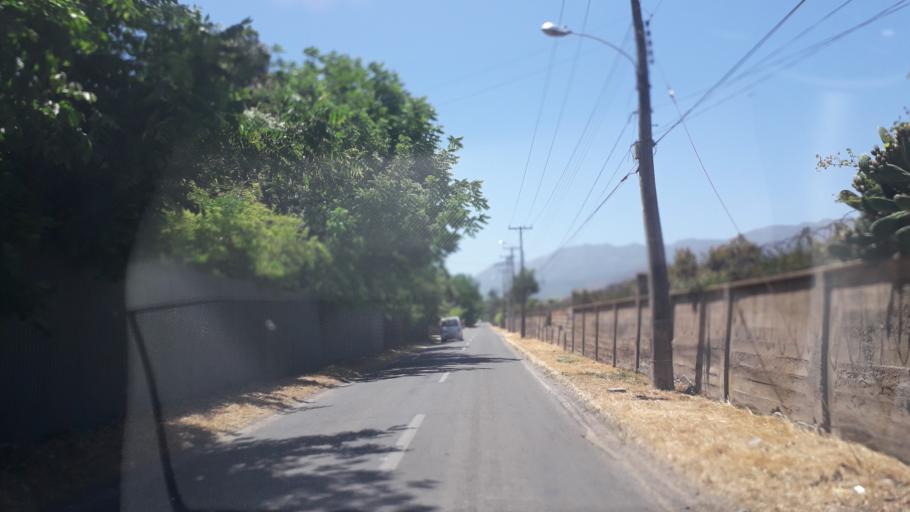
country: CL
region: Valparaiso
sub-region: Provincia de Quillota
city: Quillota
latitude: -32.9207
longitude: -71.2405
